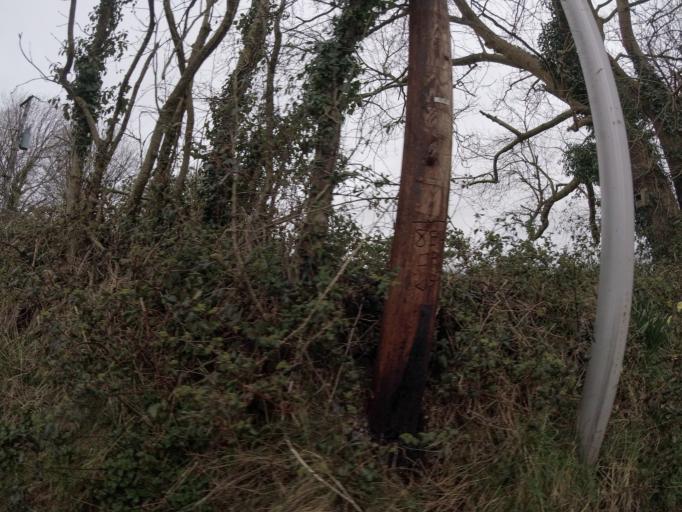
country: IE
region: Munster
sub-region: Waterford
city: Dunmore East
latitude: 52.2687
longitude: -6.9943
